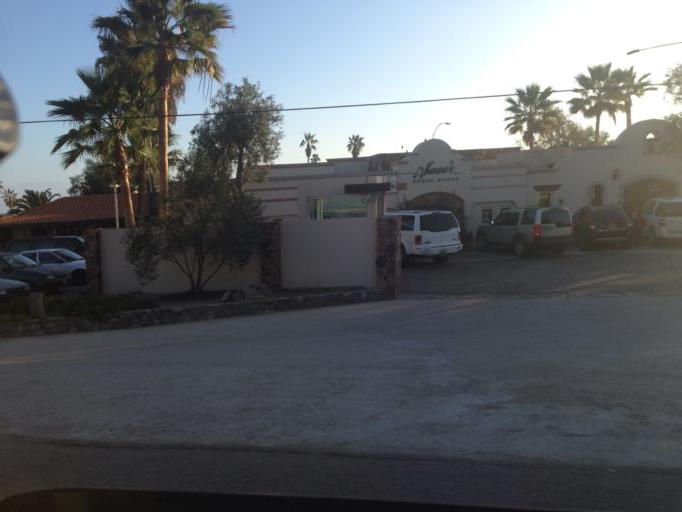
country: MX
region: Baja California
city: El Sauzal
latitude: 31.8631
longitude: -116.6540
